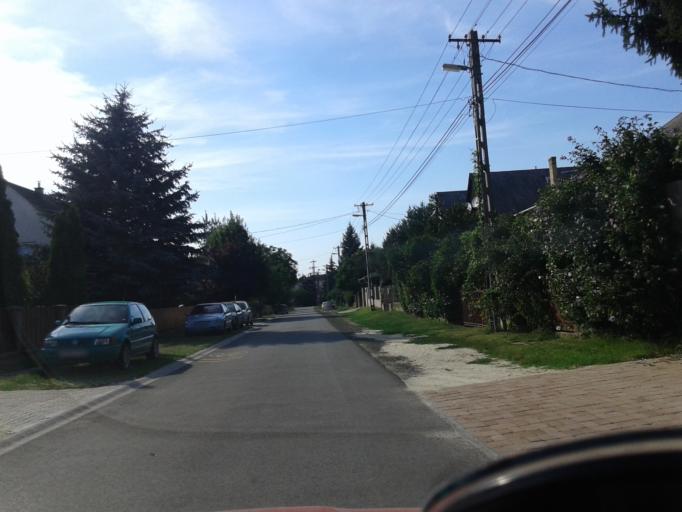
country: HU
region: Pest
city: Godollo
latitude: 47.6020
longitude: 19.3822
